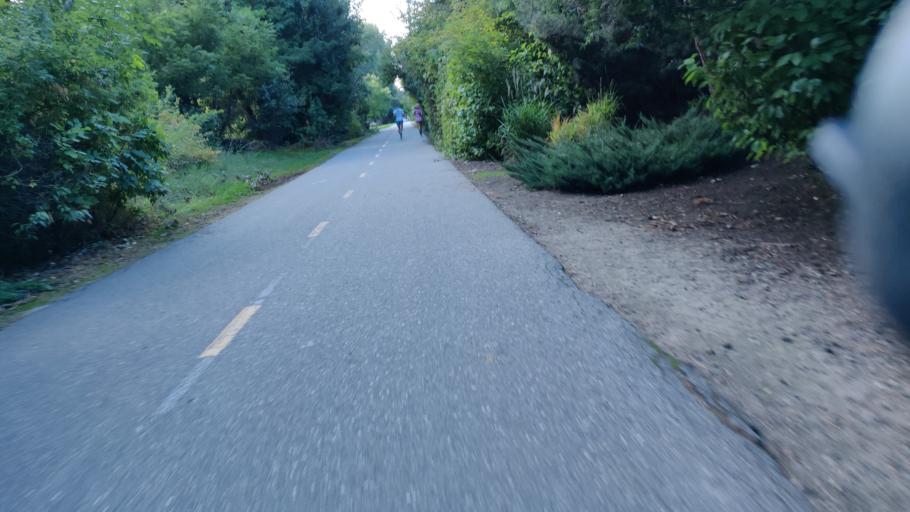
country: US
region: Idaho
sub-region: Ada County
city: Boise
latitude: 43.6017
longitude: -116.1793
